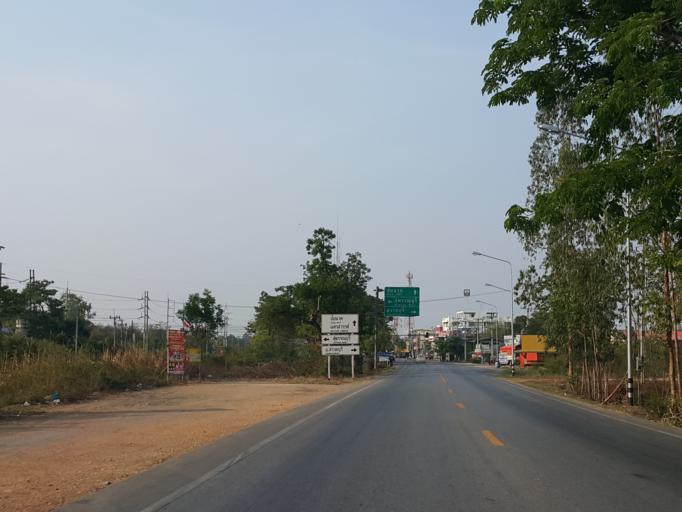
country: TH
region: Chai Nat
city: Sankhaburi
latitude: 15.0420
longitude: 100.1478
